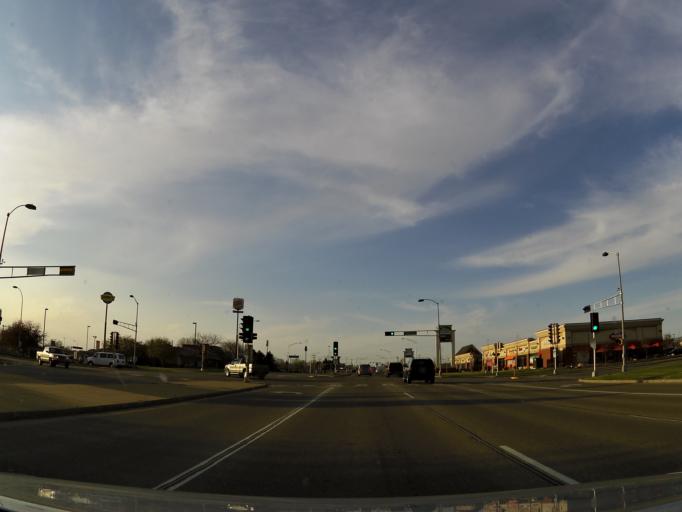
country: US
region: Wisconsin
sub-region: Saint Croix County
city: Hudson
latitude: 44.9578
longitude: -92.7214
